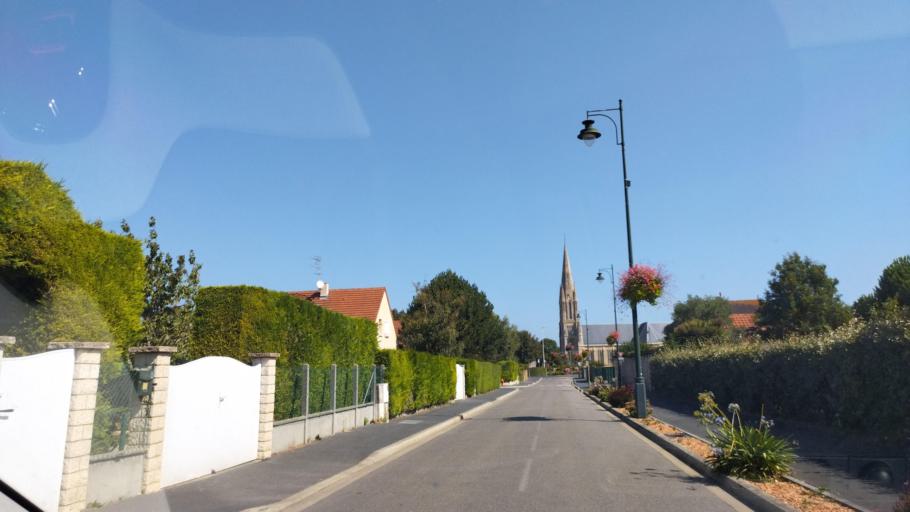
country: FR
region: Lower Normandy
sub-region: Departement du Calvados
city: Saint-Aubin-sur-Mer
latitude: 49.3266
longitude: -0.3969
